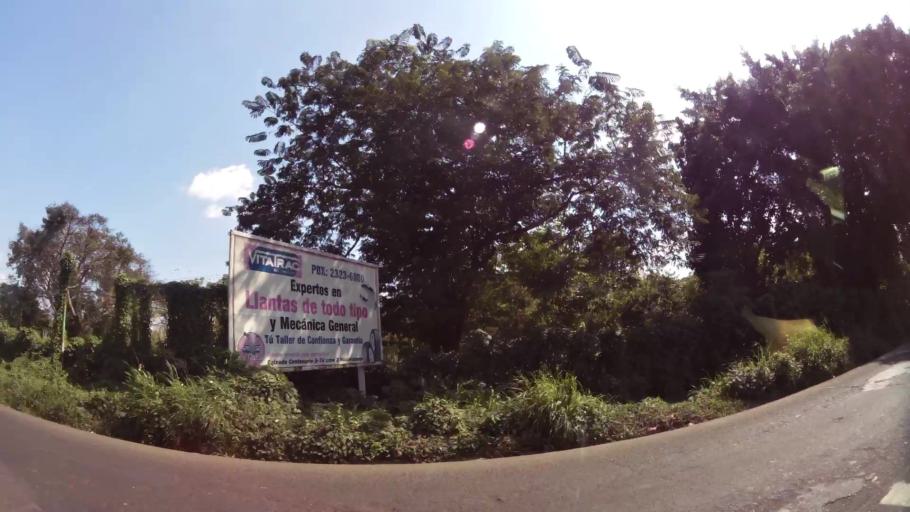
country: GT
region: Suchitepeque
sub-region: Municipio de Cuyotenango
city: Cuyotenango
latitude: 14.5441
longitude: -91.5673
